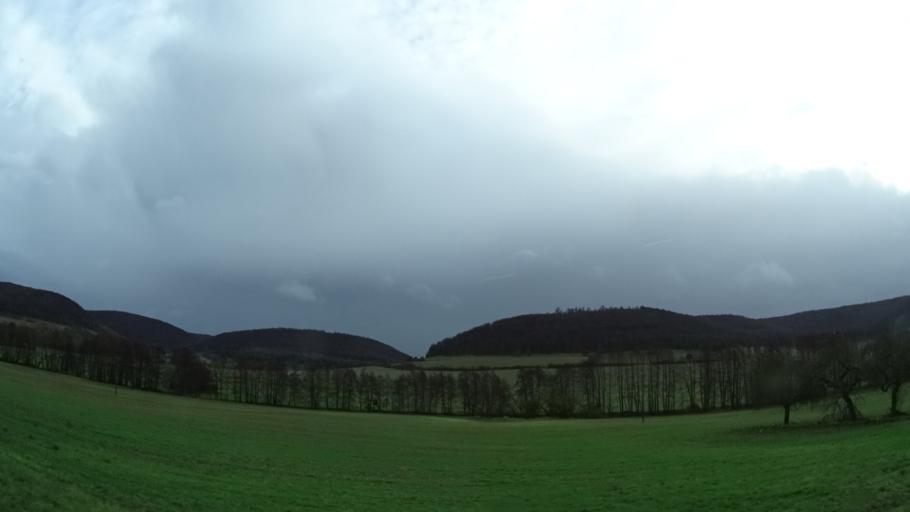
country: DE
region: Thuringia
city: Stepfershausen
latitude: 50.5711
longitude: 10.3237
